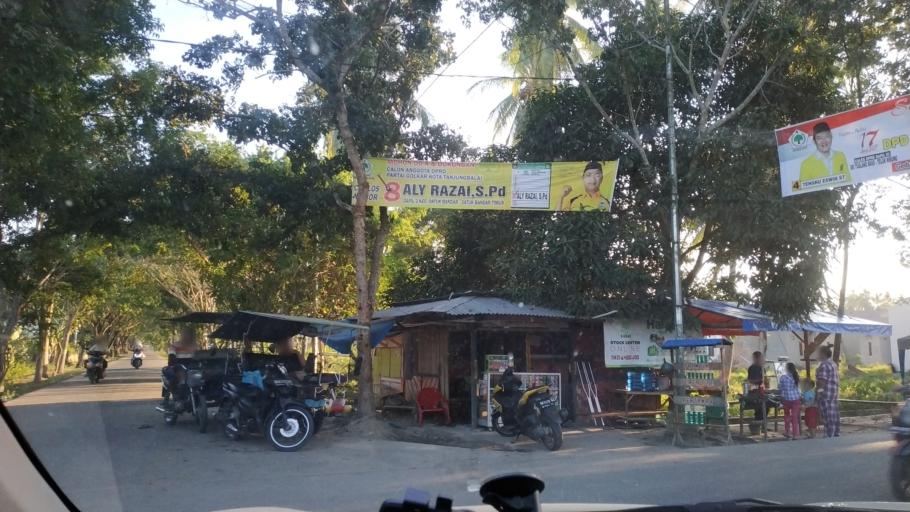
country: ID
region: North Sumatra
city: Tanjungbalai
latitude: 2.9406
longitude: 99.7880
